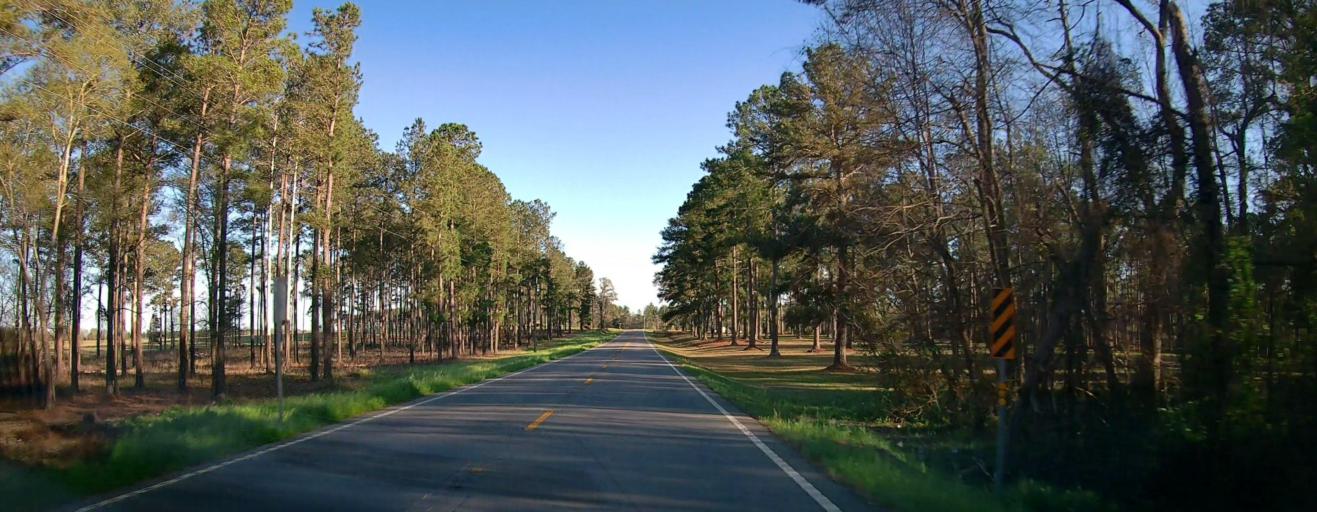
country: US
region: Georgia
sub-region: Pulaski County
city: Hawkinsville
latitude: 32.2144
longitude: -83.3835
